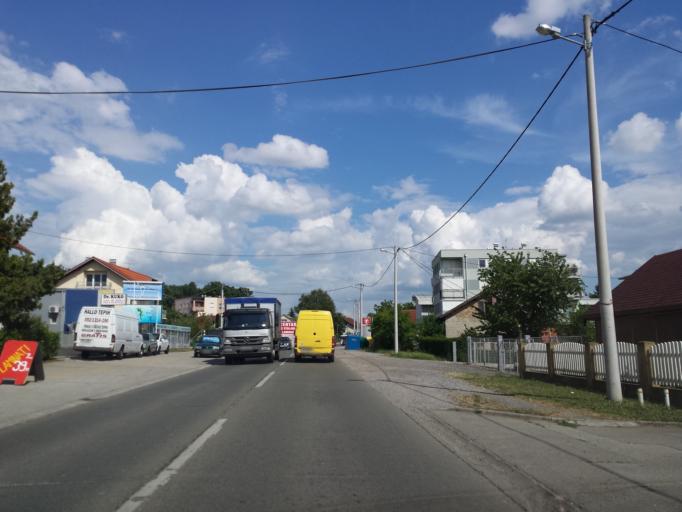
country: HR
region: Grad Zagreb
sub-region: Sesvete
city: Sesvete
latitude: 45.8235
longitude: 16.1559
